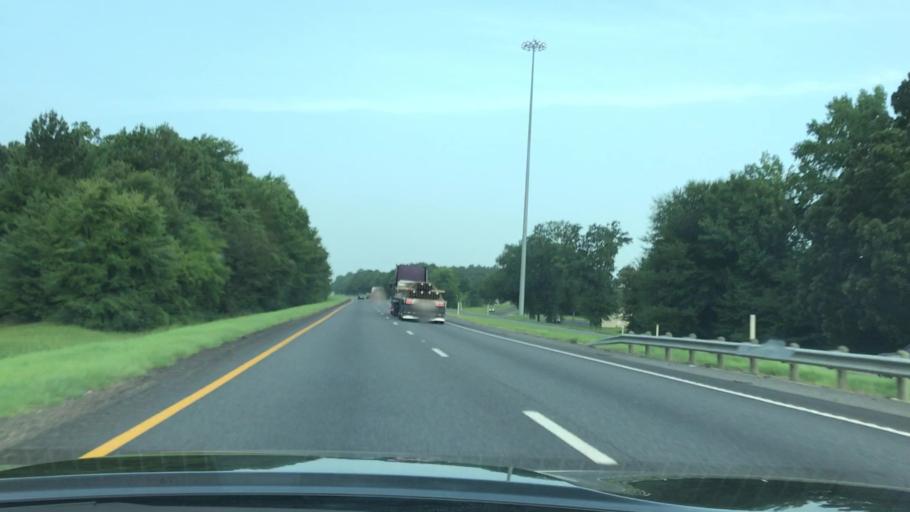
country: US
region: Texas
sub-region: Gregg County
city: Kilgore
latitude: 32.4353
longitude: -94.8287
